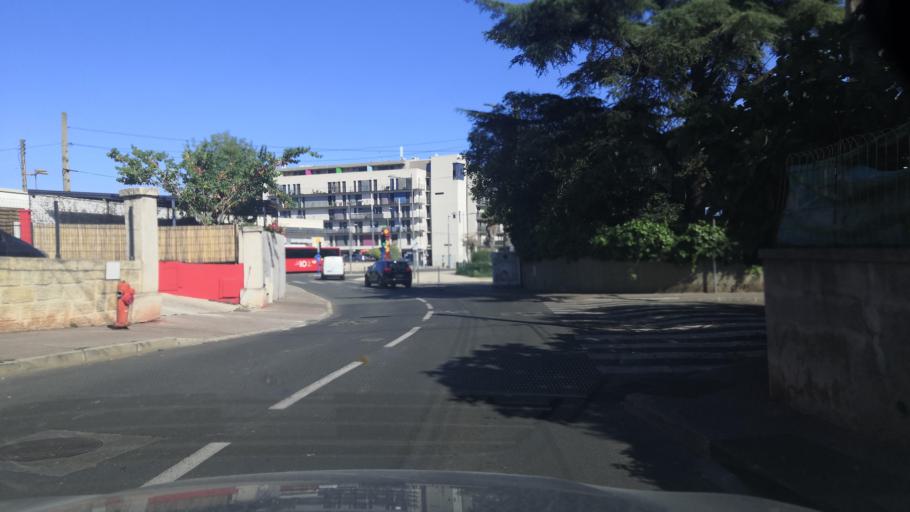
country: FR
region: Languedoc-Roussillon
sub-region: Departement de l'Herault
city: Montpellier
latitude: 43.5914
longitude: 3.8892
